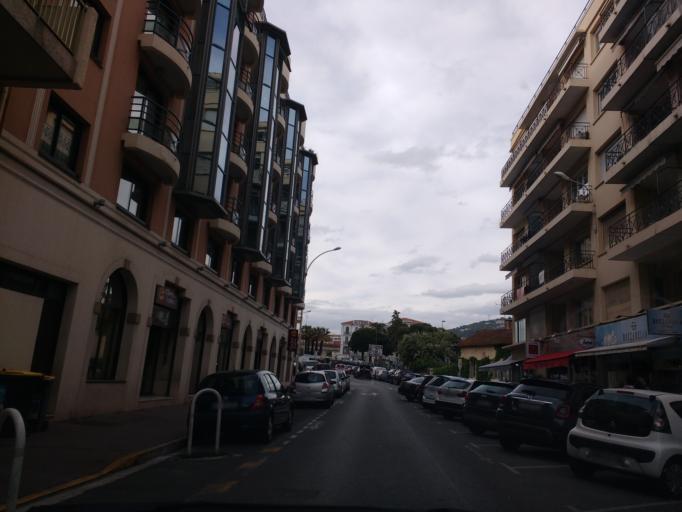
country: FR
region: Provence-Alpes-Cote d'Azur
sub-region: Departement des Alpes-Maritimes
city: Cannes
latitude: 43.5495
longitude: 7.0305
